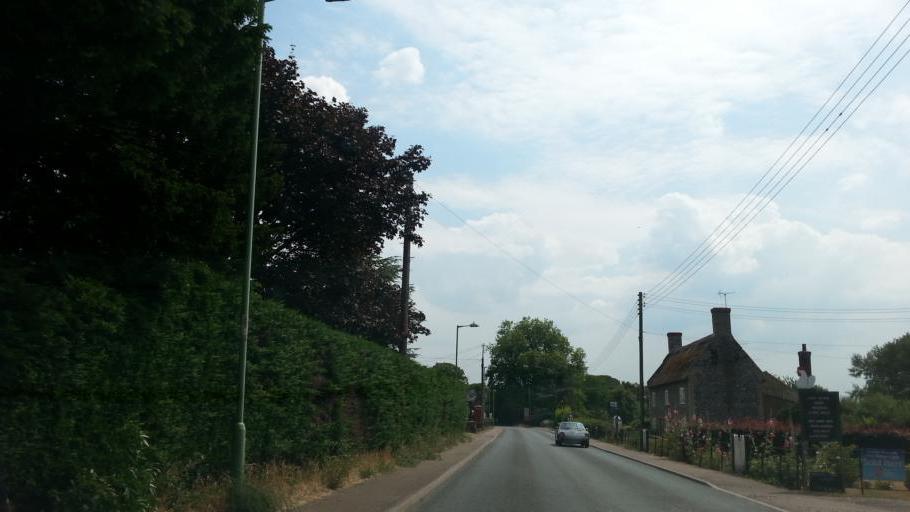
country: GB
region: England
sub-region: Suffolk
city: Lakenheath
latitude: 52.3751
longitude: 0.5290
